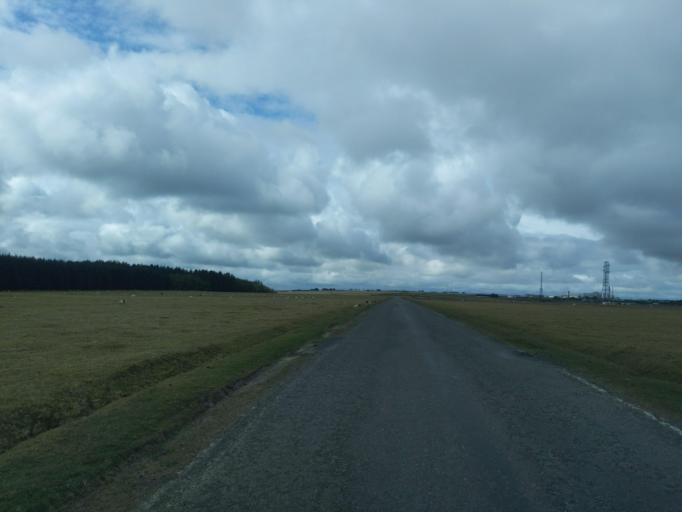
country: GB
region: England
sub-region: Cornwall
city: Camelford
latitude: 50.6366
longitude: -4.6205
